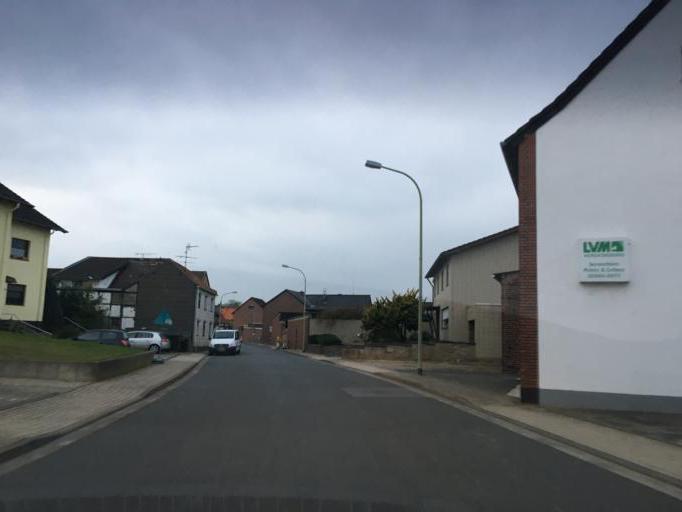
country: DE
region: North Rhine-Westphalia
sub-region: Regierungsbezirk Koln
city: Vettweiss
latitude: 50.7640
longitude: 6.5620
